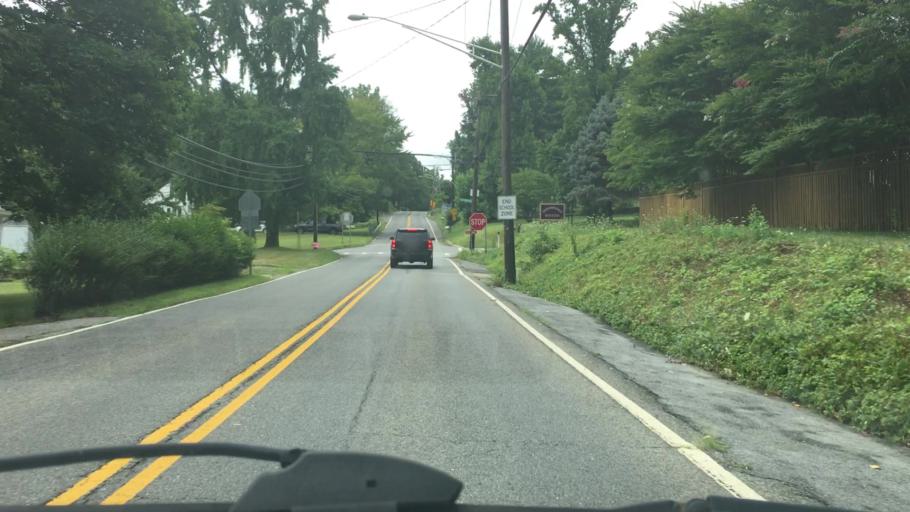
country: US
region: Maryland
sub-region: Prince George's County
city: Glenn Dale
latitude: 38.9828
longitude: -76.7722
